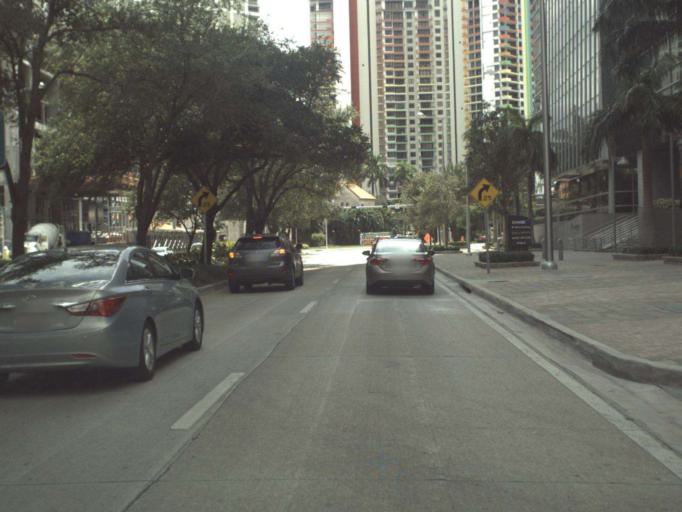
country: US
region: Florida
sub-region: Miami-Dade County
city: Miami
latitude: 25.7592
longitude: -80.1926
